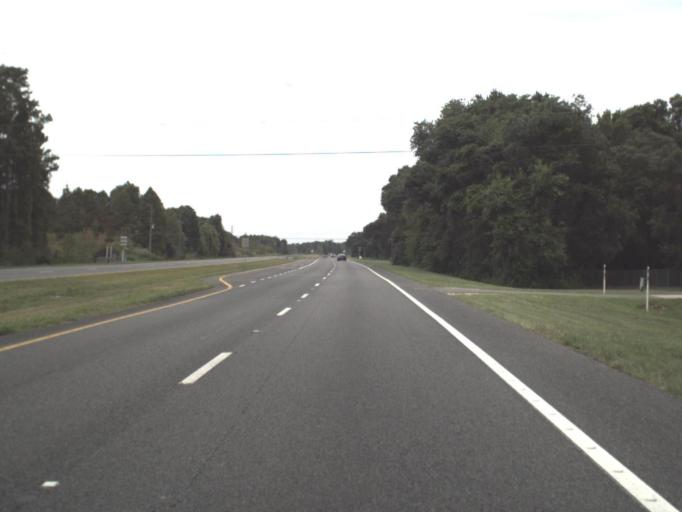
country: US
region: Florida
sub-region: Citrus County
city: Inverness
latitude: 28.8508
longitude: -82.2421
